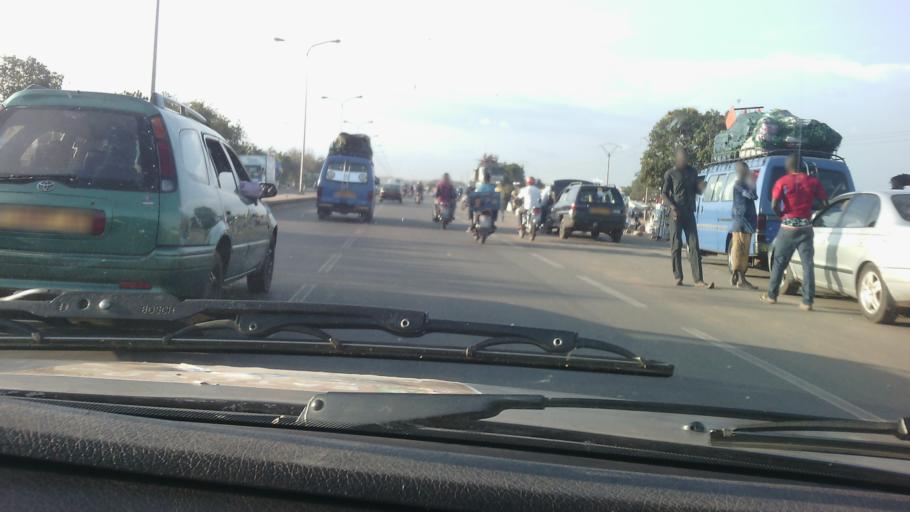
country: TG
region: Maritime
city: Lome
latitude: 6.2410
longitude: 1.2102
